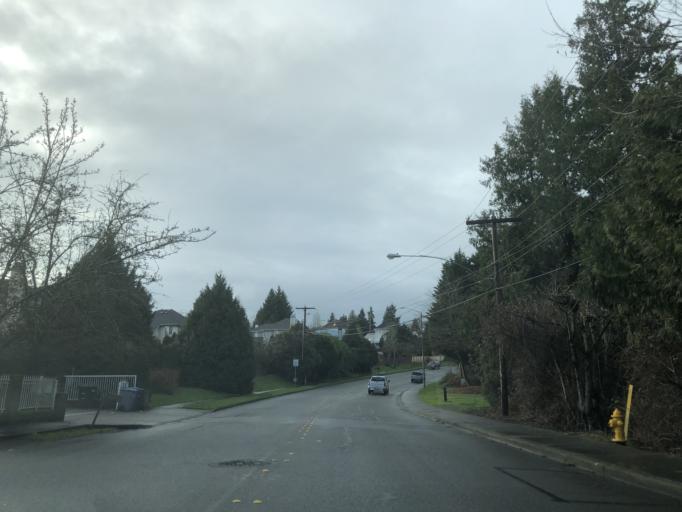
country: US
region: Washington
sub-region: King County
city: SeaTac
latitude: 47.4439
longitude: -122.2703
